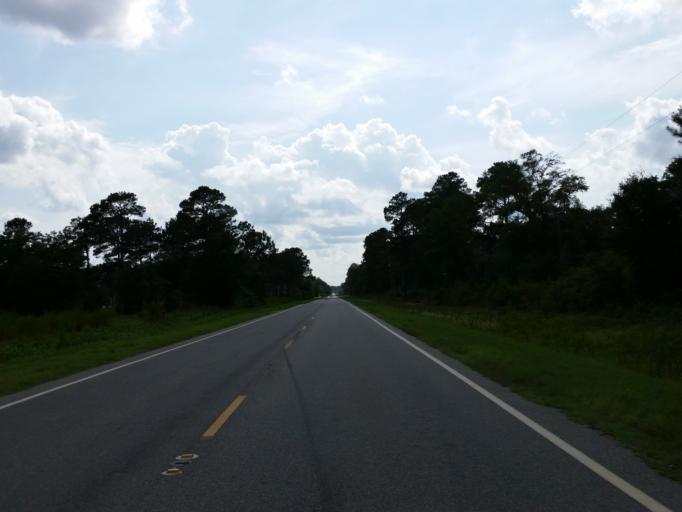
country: US
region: Georgia
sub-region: Lee County
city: Leesburg
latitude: 31.7271
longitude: -83.9791
